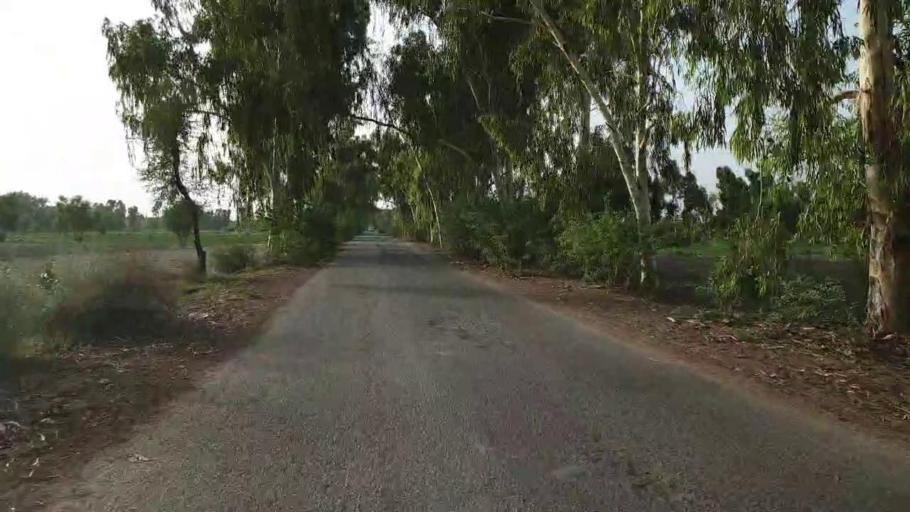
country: PK
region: Sindh
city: Bozdar
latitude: 27.1161
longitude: 68.9575
